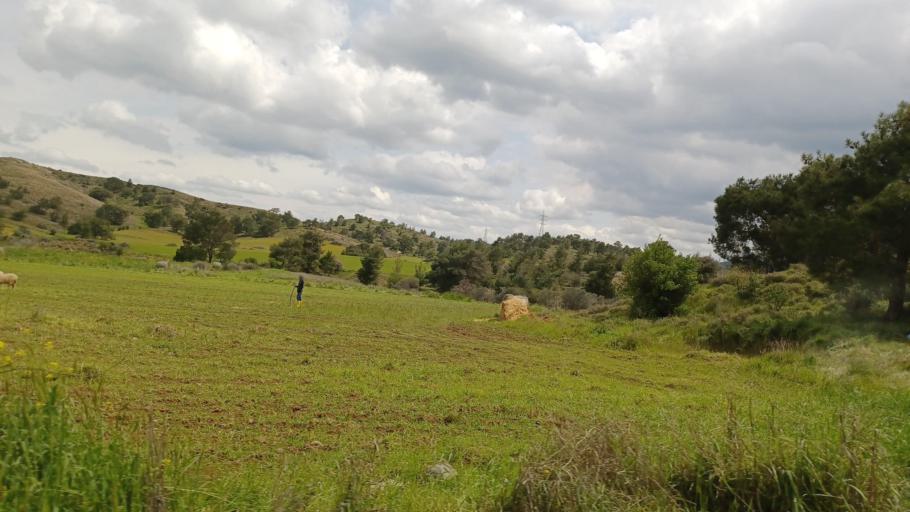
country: CY
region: Lefkosia
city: Lefka
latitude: 35.0733
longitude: 32.9261
